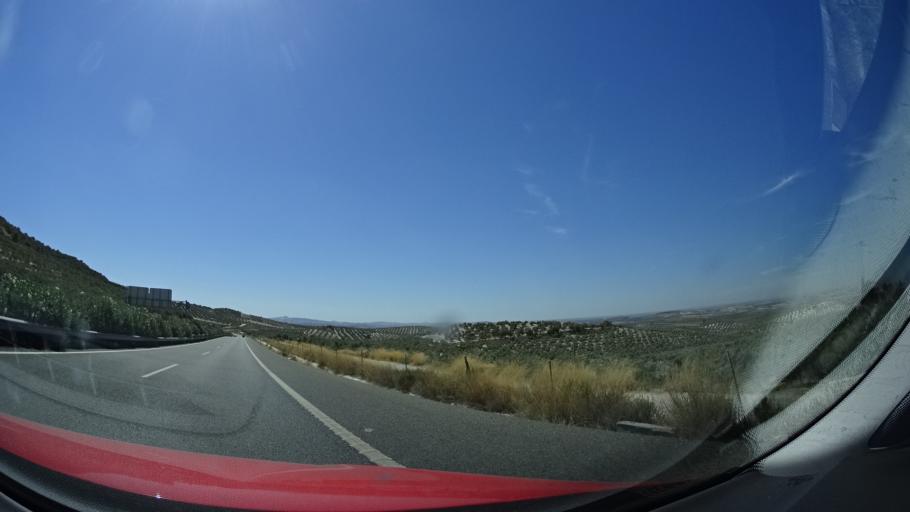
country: ES
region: Andalusia
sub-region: Provincia de Sevilla
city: Estepa
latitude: 37.2897
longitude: -4.9088
